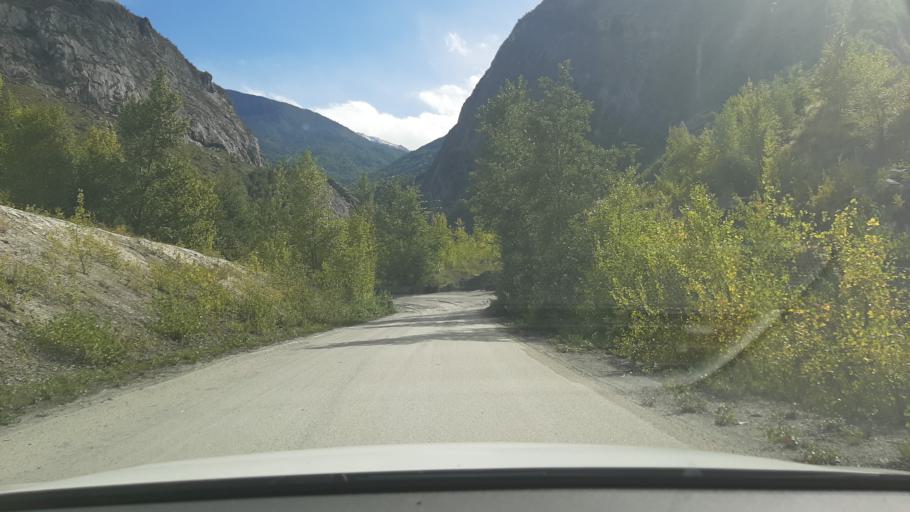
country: FR
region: Rhone-Alpes
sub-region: Departement de la Savoie
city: Saint-Michel-de-Maurienne
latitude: 45.2286
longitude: 6.4470
